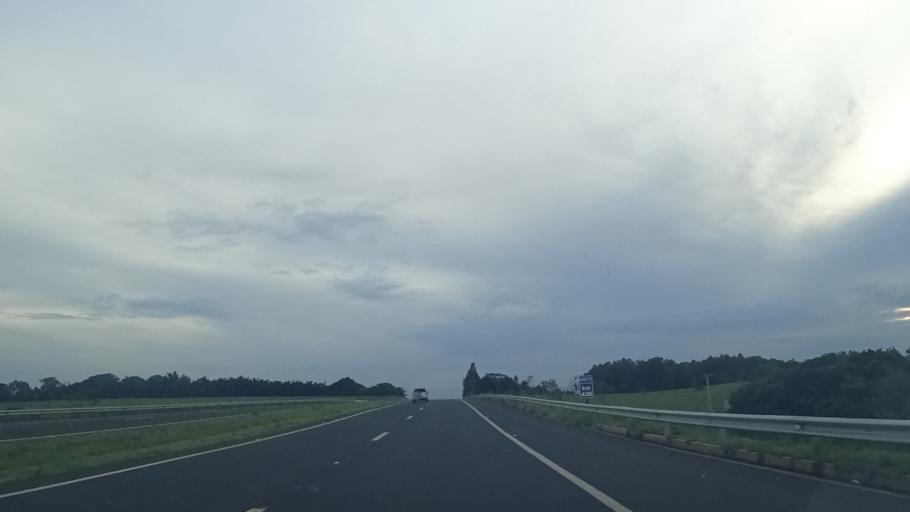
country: BR
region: Sao Paulo
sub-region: Martinopolis
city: Martinopolis
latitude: -22.1480
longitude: -51.2538
